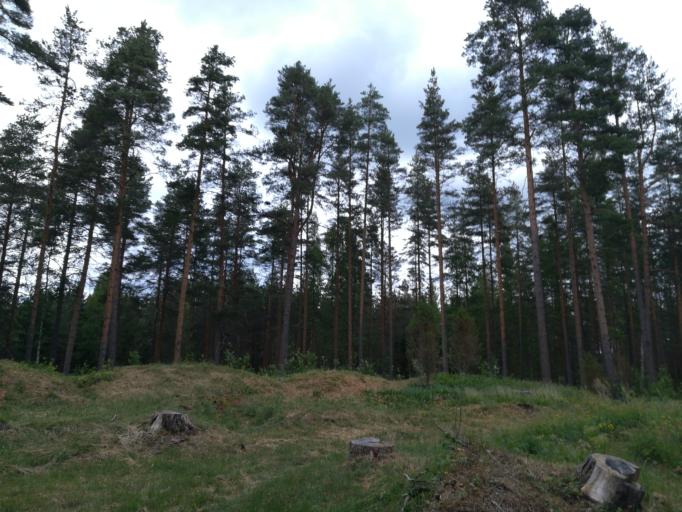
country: FI
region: South Karelia
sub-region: Lappeenranta
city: Savitaipale
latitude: 61.2585
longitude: 27.7091
